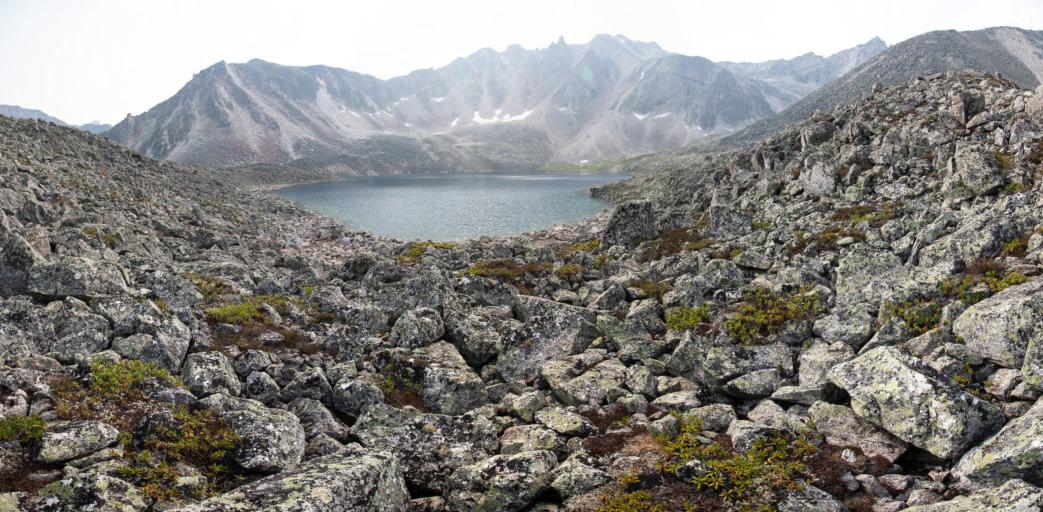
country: RU
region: Respublika Buryatiya
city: Novyy Uoyan
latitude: 56.2144
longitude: 111.0241
